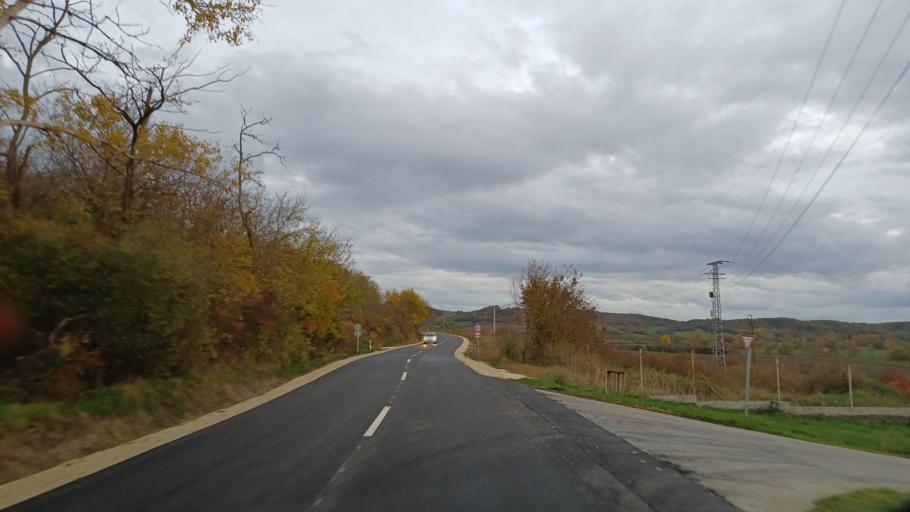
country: HU
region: Tolna
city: Gyonk
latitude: 46.5934
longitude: 18.4301
